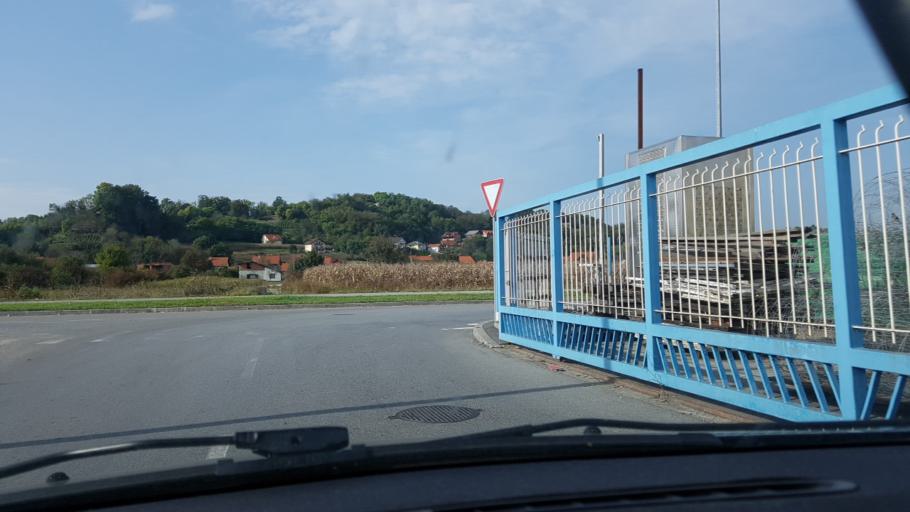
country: HR
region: Krapinsko-Zagorska
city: Zabok
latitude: 46.0148
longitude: 15.8850
